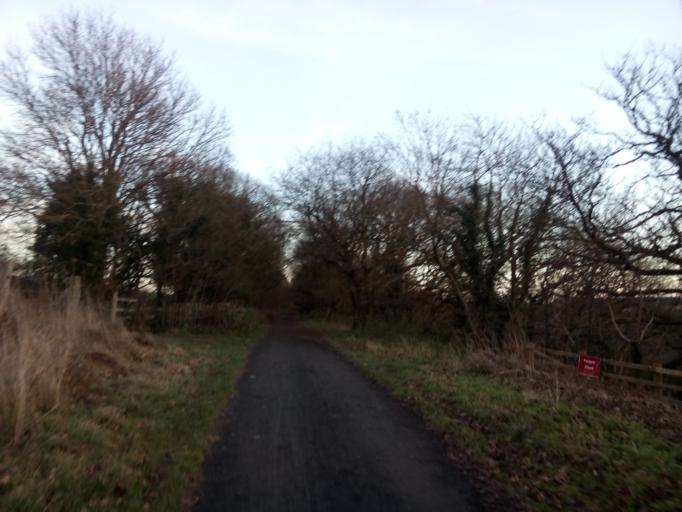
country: GB
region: England
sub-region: County Durham
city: Ushaw Moor
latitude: 54.7697
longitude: -1.6281
